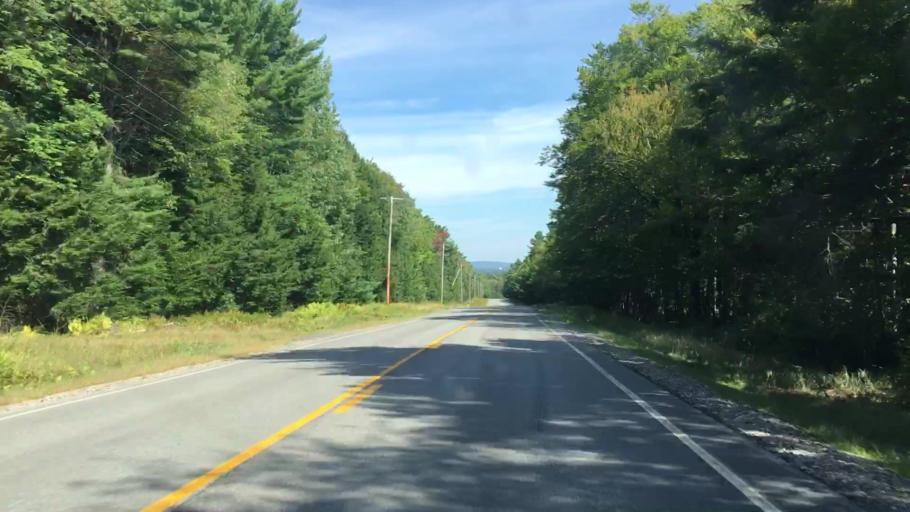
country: US
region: Maine
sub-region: Penobscot County
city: Howland
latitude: 45.2334
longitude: -68.7522
